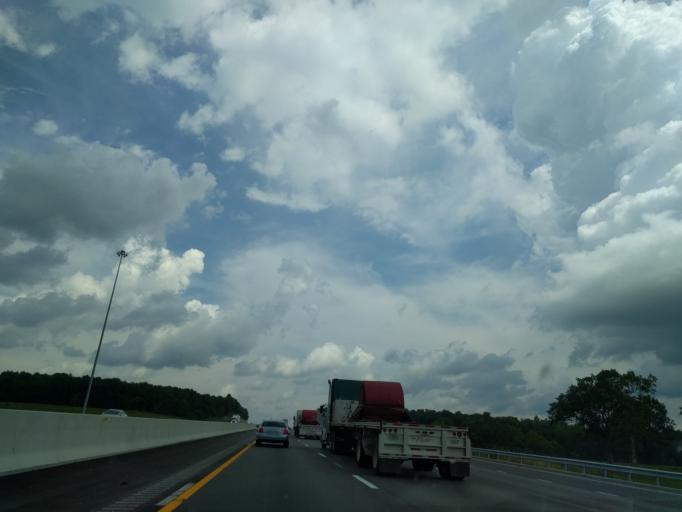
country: US
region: Kentucky
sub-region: Larue County
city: Hodgenville
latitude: 37.4632
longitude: -85.8824
